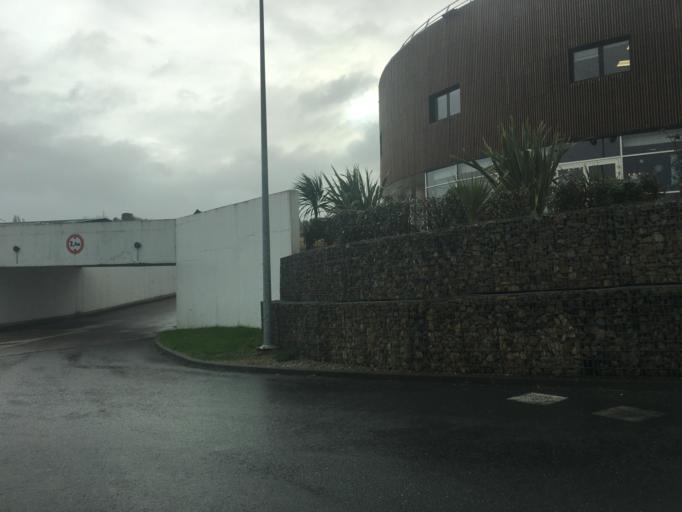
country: FR
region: Lower Normandy
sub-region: Departement de la Manche
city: Tourlaville
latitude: 49.6324
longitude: -1.5898
